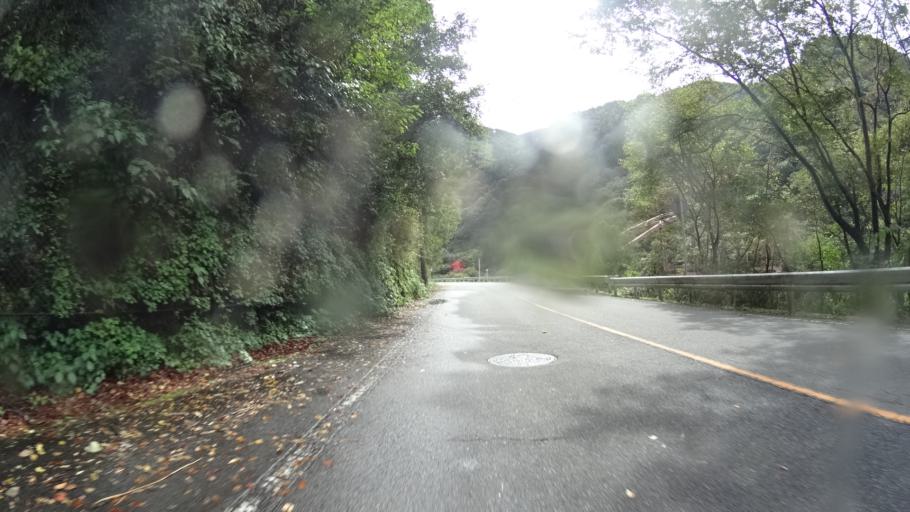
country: JP
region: Yamanashi
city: Otsuki
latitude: 35.7805
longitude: 138.9791
